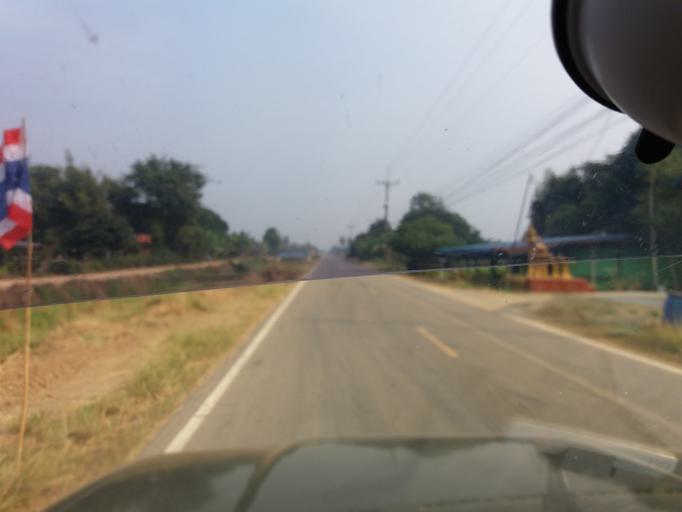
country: TH
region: Suphan Buri
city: Doem Bang Nang Buat
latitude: 14.8805
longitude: 100.1785
